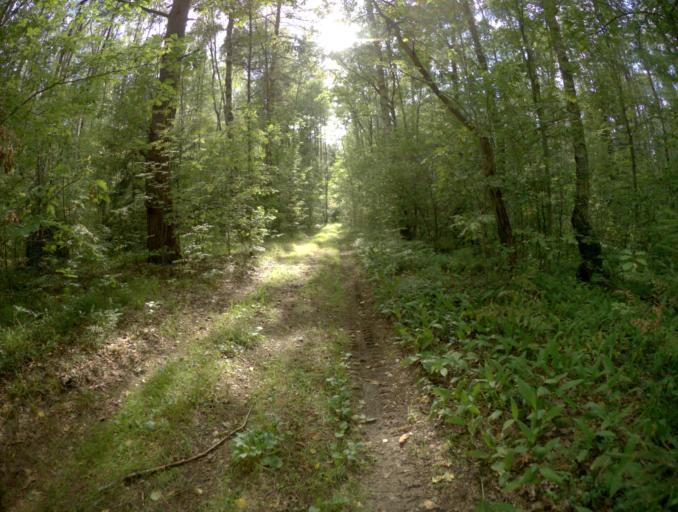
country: RU
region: Vladimir
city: Orgtrud
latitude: 56.1324
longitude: 40.6094
